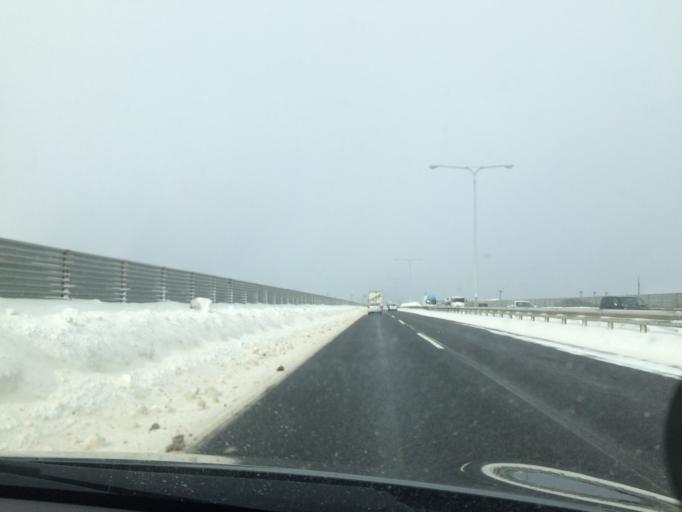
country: JP
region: Hokkaido
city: Sapporo
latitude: 43.0384
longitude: 141.4399
